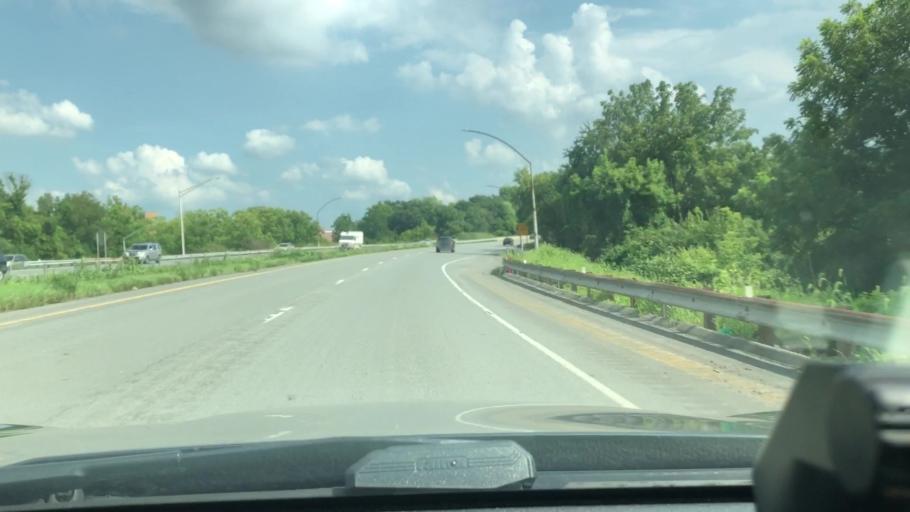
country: US
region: Pennsylvania
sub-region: Northampton County
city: Bethlehem
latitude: 40.6268
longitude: -75.3879
